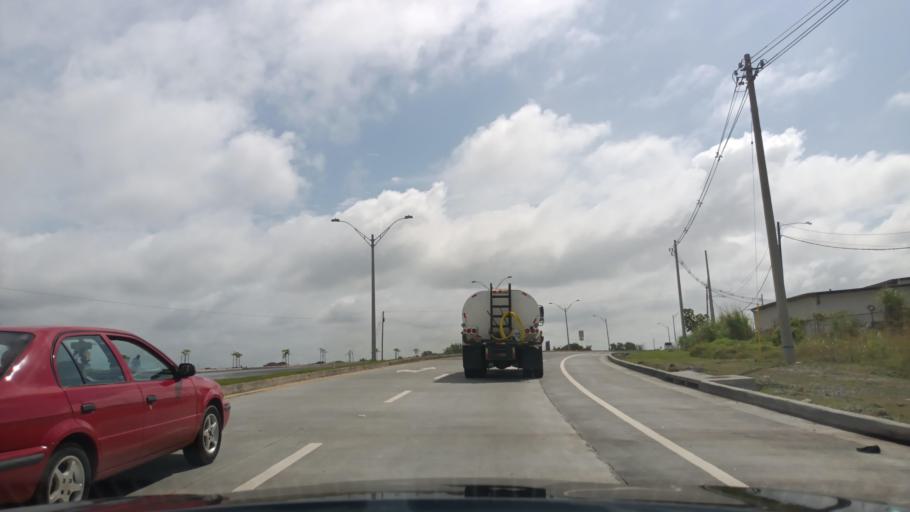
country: PA
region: Panama
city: San Miguelito
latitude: 9.0962
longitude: -79.4667
